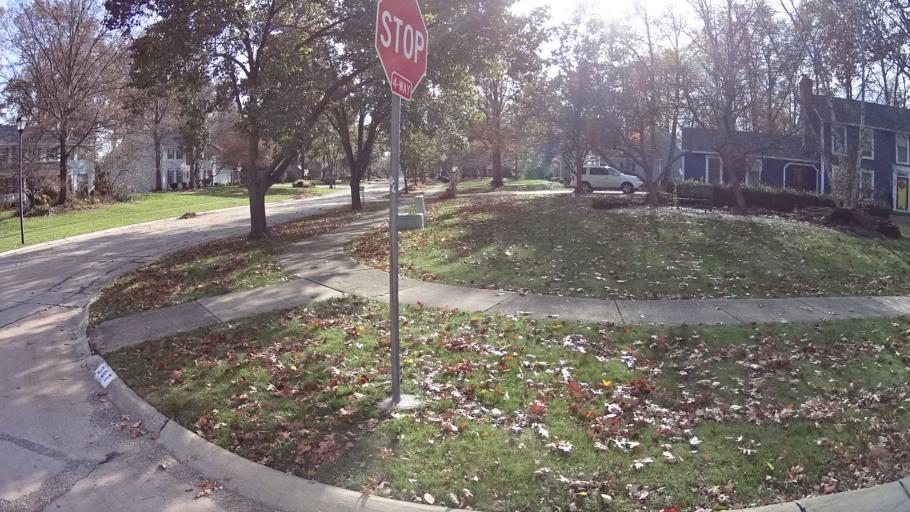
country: US
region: Ohio
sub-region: Lorain County
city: Avon Lake
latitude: 41.5006
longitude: -81.9809
